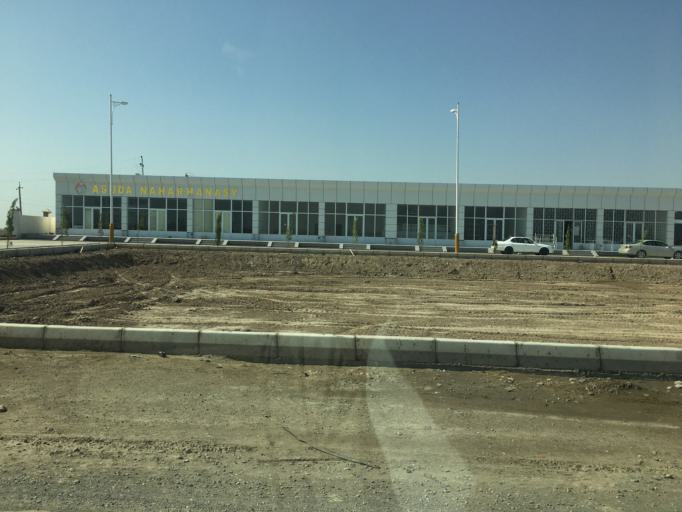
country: TM
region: Lebap
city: Turkmenabat
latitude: 39.0105
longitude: 63.6050
